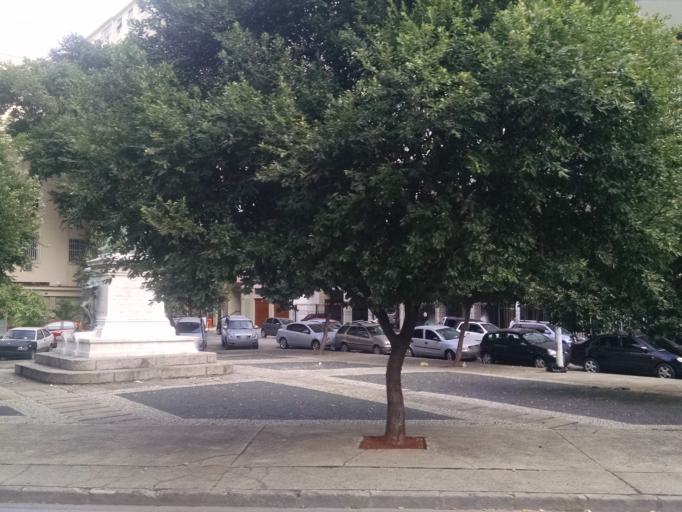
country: BR
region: Rio de Janeiro
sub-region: Rio De Janeiro
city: Rio de Janeiro
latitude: -22.9617
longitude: -43.1757
